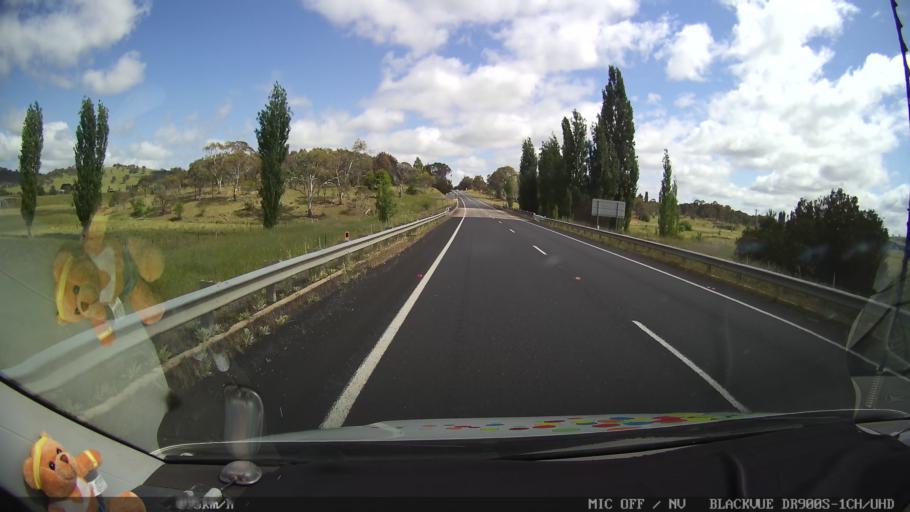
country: AU
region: New South Wales
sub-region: Glen Innes Severn
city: Glen Innes
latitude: -29.9348
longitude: 151.7238
